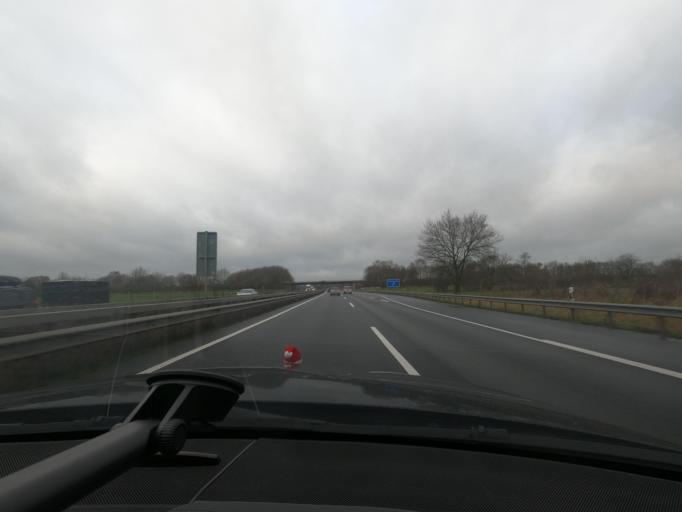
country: DE
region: Schleswig-Holstein
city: Schonbek
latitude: 54.1783
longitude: 9.9517
